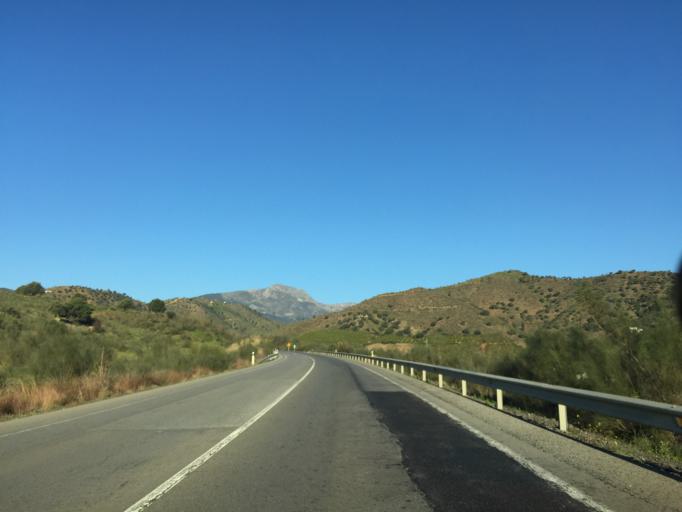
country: ES
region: Andalusia
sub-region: Provincia de Malaga
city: Alora
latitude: 36.8028
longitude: -4.7601
